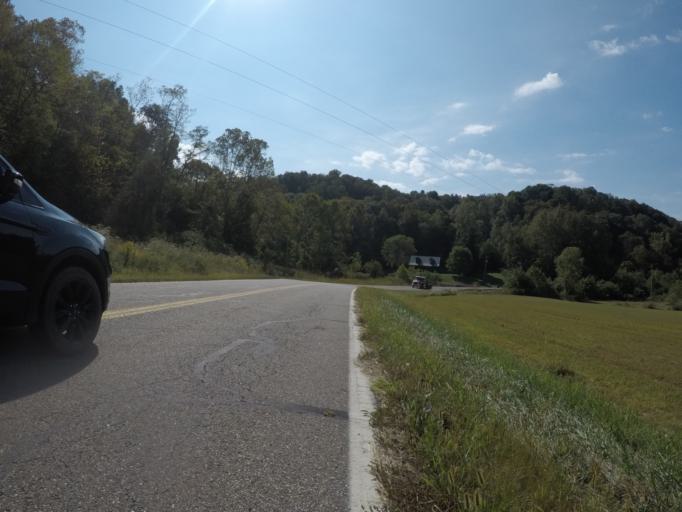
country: US
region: West Virginia
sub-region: Cabell County
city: Lesage
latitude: 38.6359
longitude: -82.4307
